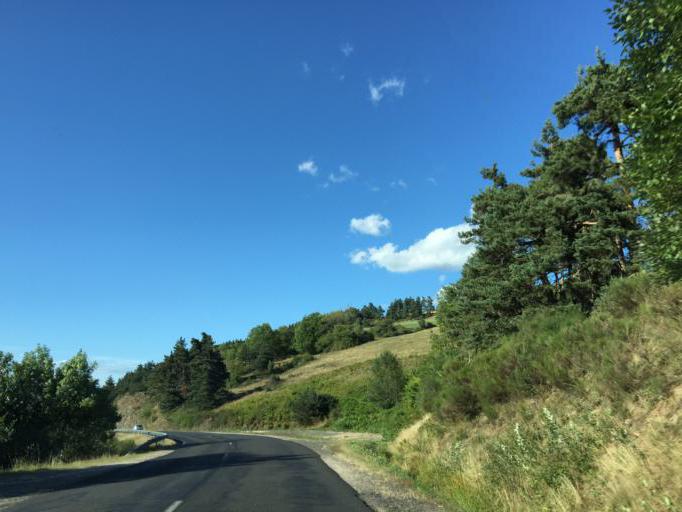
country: FR
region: Auvergne
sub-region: Departement de la Haute-Loire
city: Saugues
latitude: 44.9721
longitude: 3.6135
